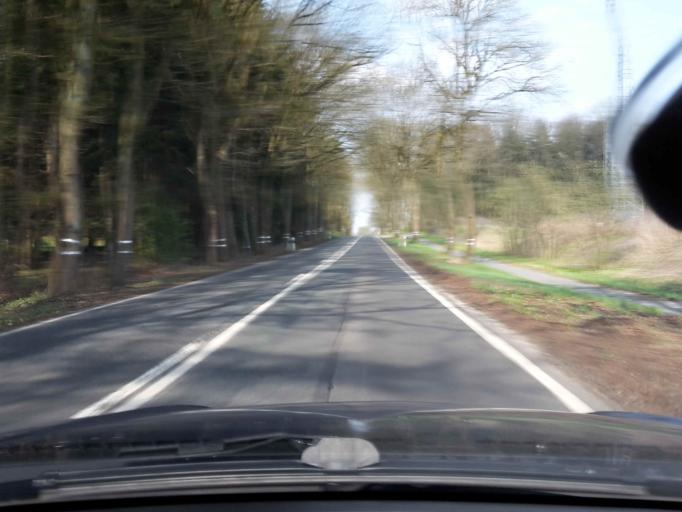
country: DE
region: Lower Saxony
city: Harmstorf
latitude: 53.3564
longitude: 9.9901
